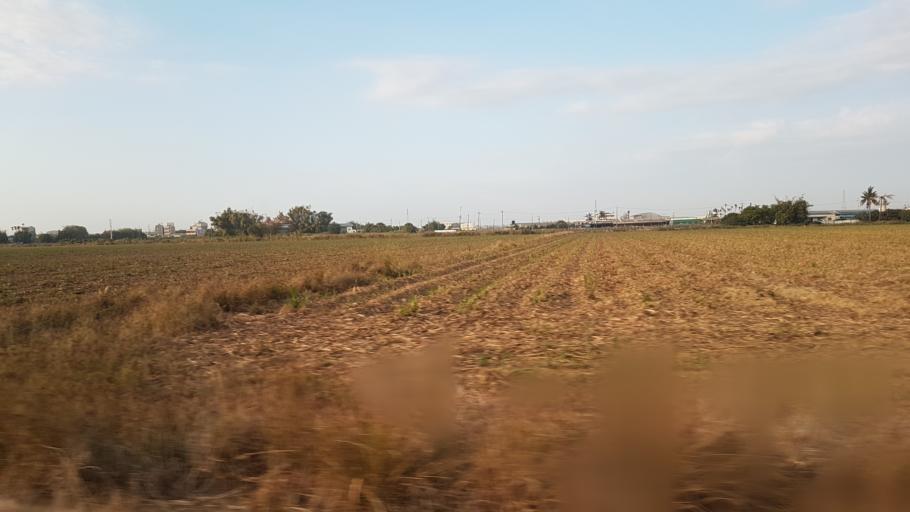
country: TW
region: Taiwan
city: Xinying
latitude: 23.3468
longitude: 120.3711
